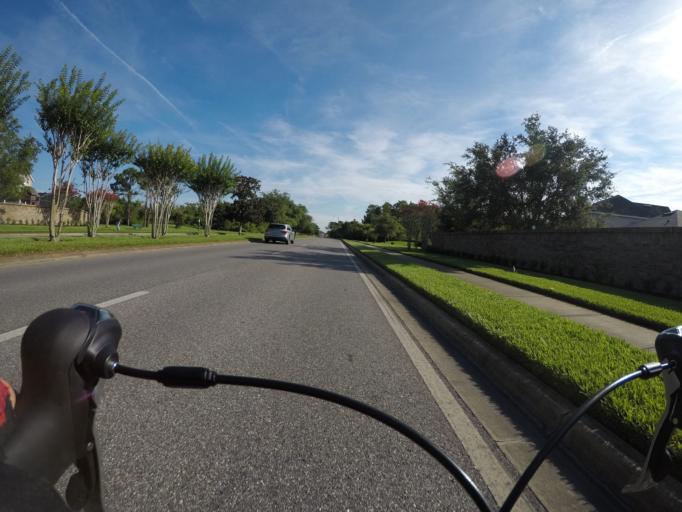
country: US
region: Florida
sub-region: Osceola County
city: Buenaventura Lakes
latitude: 28.3585
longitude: -81.3489
